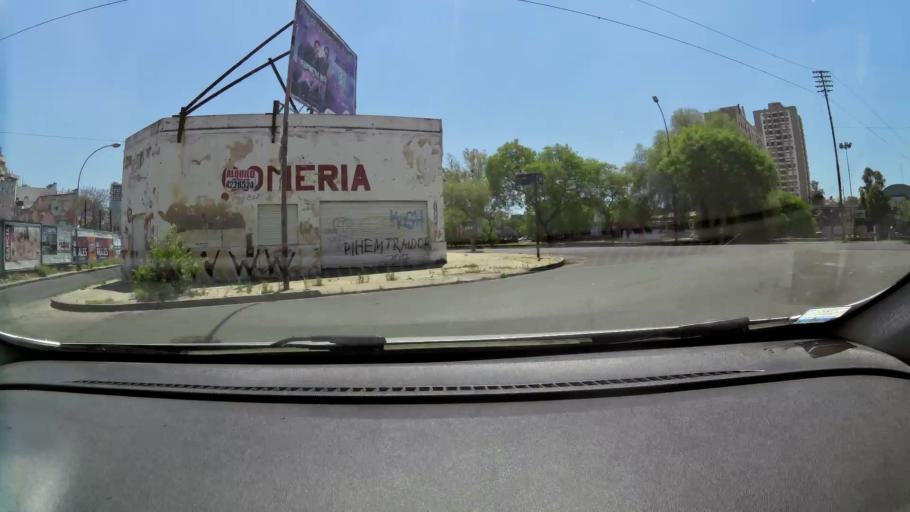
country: AR
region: Cordoba
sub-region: Departamento de Capital
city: Cordoba
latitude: -31.4065
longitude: -64.1815
